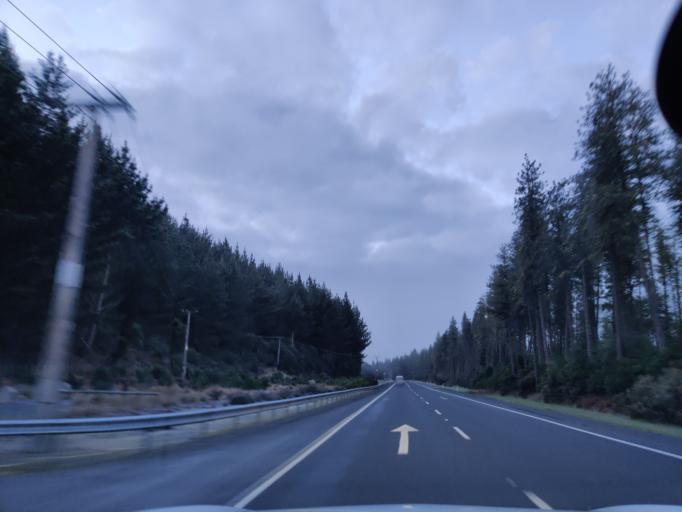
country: NZ
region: Waikato
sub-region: South Waikato District
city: Tokoroa
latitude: -38.3781
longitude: 176.0016
